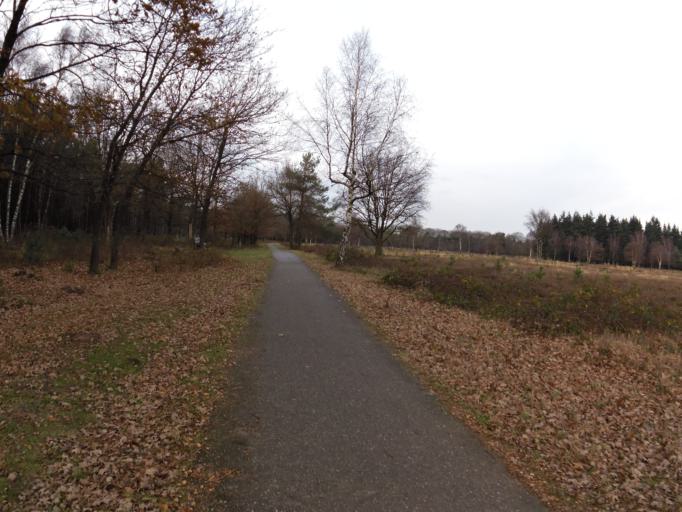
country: NL
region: North Brabant
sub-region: Gemeente Oss
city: Berghem
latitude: 51.7177
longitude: 5.5791
